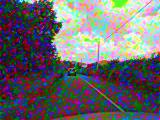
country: IE
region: Ulster
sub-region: County Donegal
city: Ramelton
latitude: 55.2014
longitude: -7.6381
